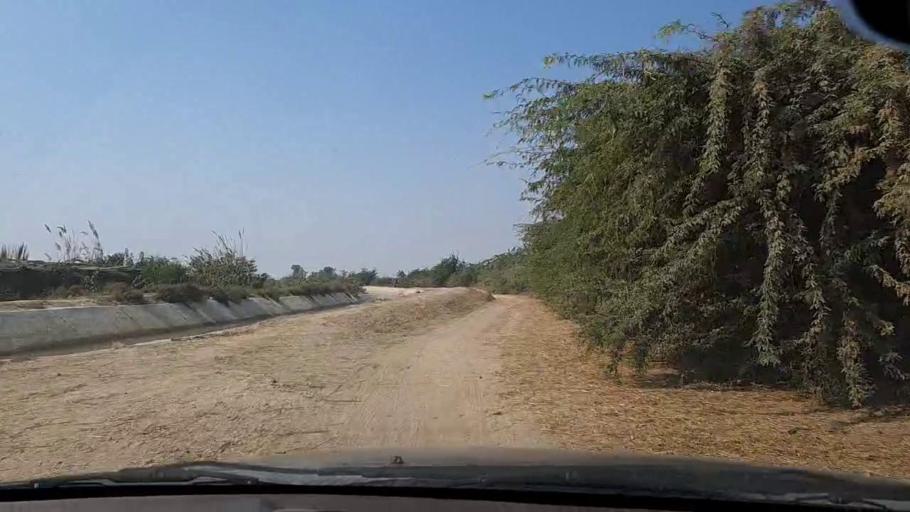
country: PK
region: Sindh
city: Chuhar Jamali
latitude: 24.4269
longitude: 67.8125
